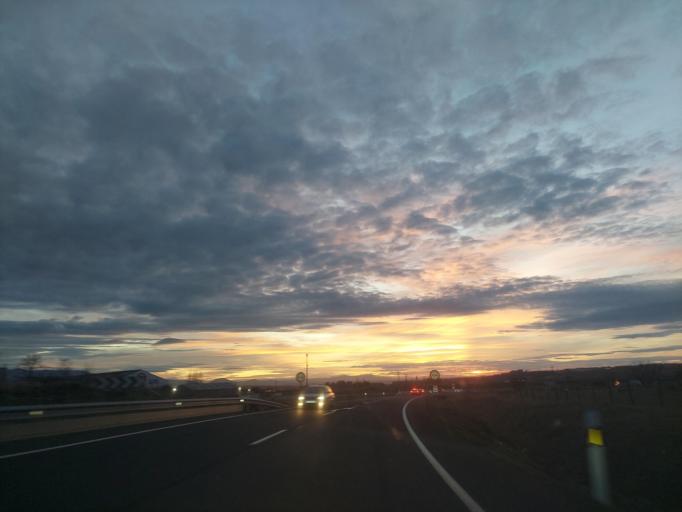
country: ES
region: Castille and Leon
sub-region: Provincia de Segovia
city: San Cristobal de Segovia
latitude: 40.9737
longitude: -4.0800
